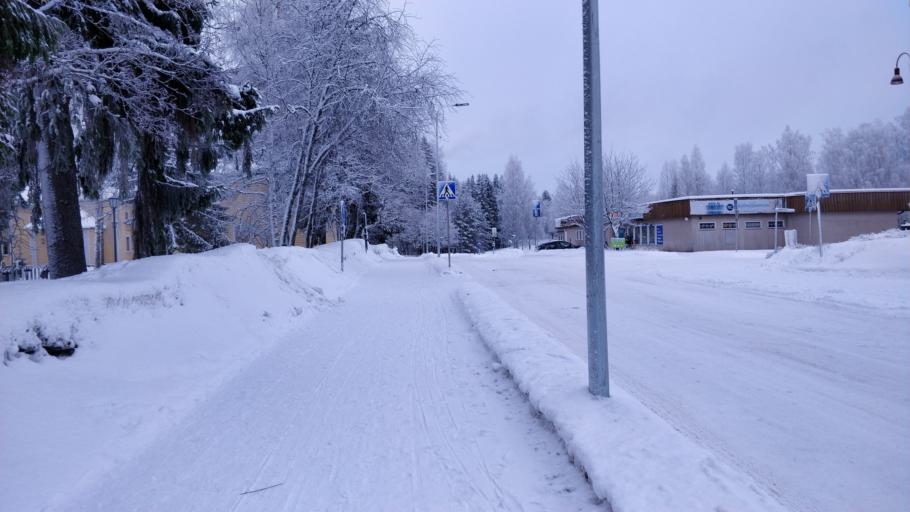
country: FI
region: Southern Savonia
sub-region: Mikkeli
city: Puumala
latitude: 61.5236
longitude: 28.1777
